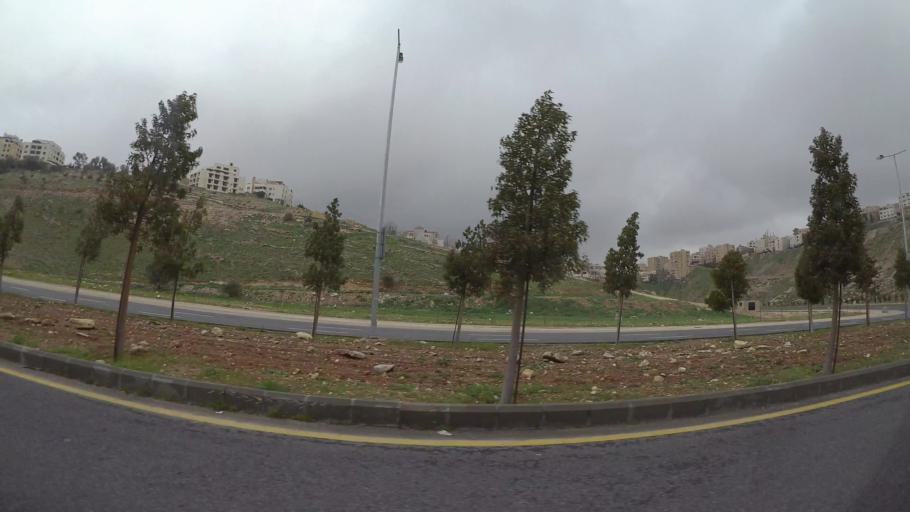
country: JO
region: Amman
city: Al Bunayyat ash Shamaliyah
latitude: 31.9309
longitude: 35.8912
